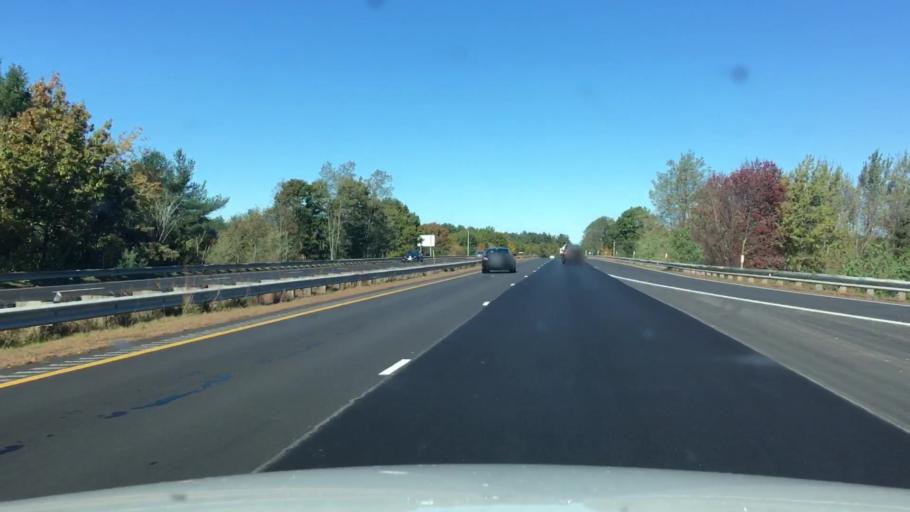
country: US
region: New Hampshire
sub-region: Strafford County
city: Dover
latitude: 43.1884
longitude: -70.8897
